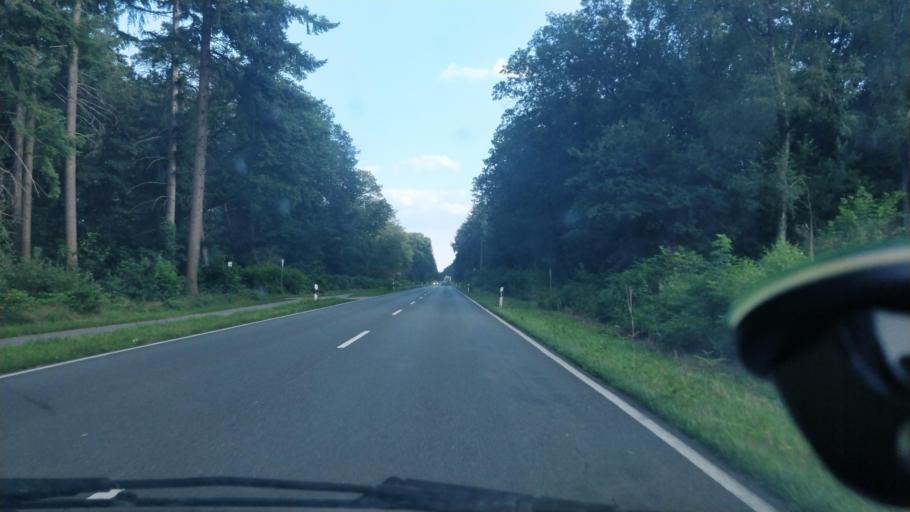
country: DE
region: North Rhine-Westphalia
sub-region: Regierungsbezirk Dusseldorf
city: Alpen
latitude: 51.5470
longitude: 6.5037
